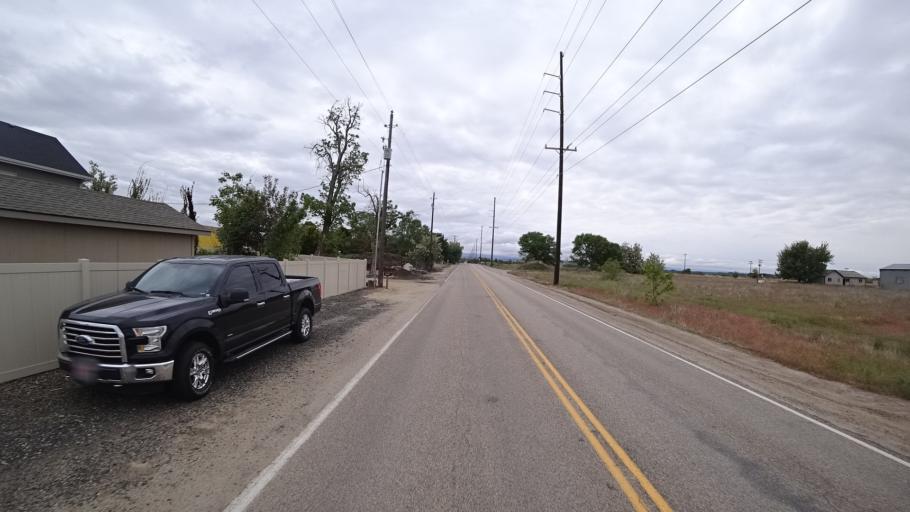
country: US
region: Idaho
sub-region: Ada County
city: Star
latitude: 43.7211
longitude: -116.4352
